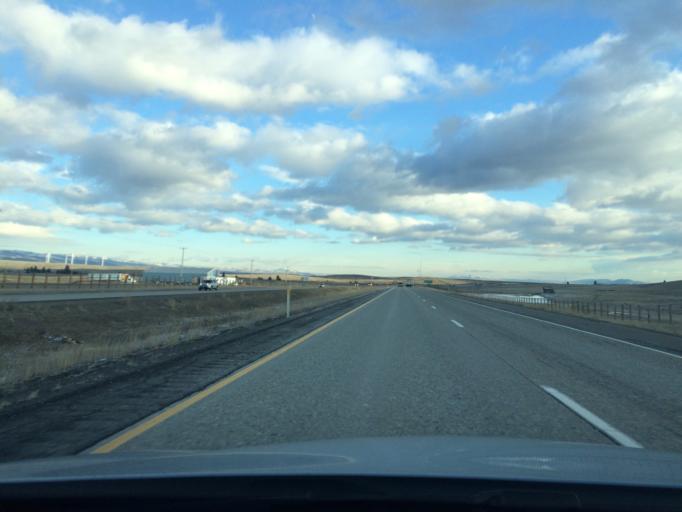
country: US
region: Washington
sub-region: Kittitas County
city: Cle Elum
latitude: 47.1108
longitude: -120.7789
